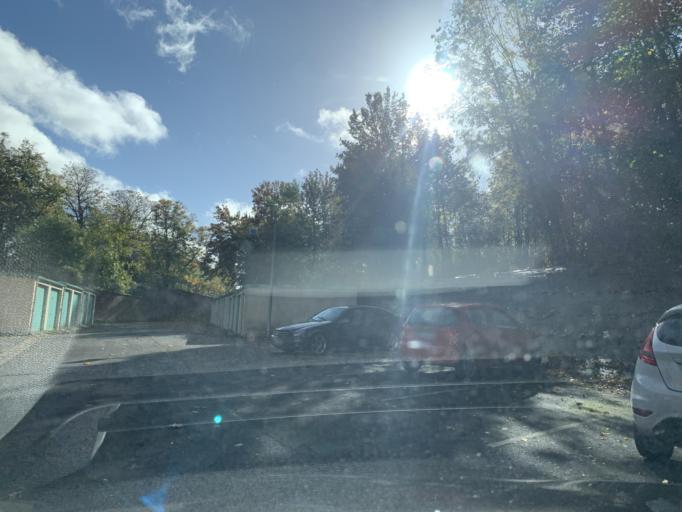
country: FR
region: Nord-Pas-de-Calais
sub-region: Departement du Nord
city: Neuville-Saint-Remy
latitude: 50.1804
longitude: 3.2364
